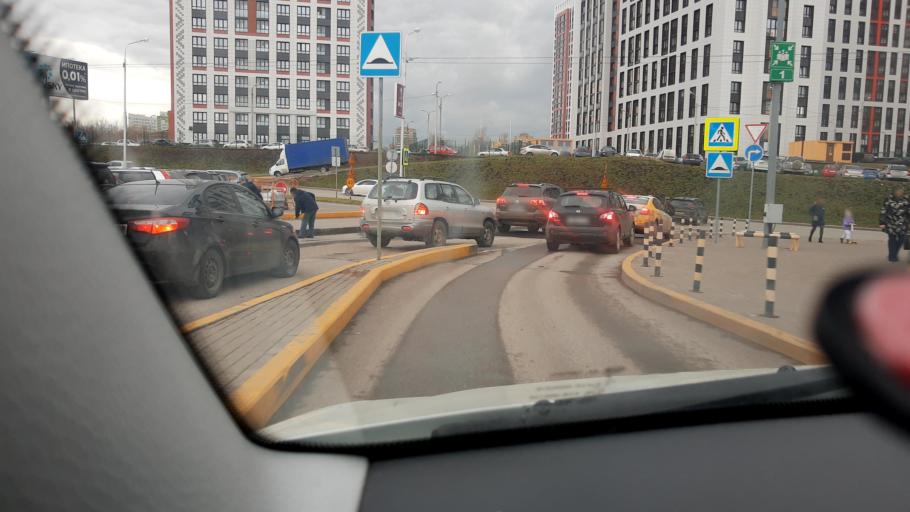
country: RU
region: Bashkortostan
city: Ufa
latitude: 54.7576
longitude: 56.0337
